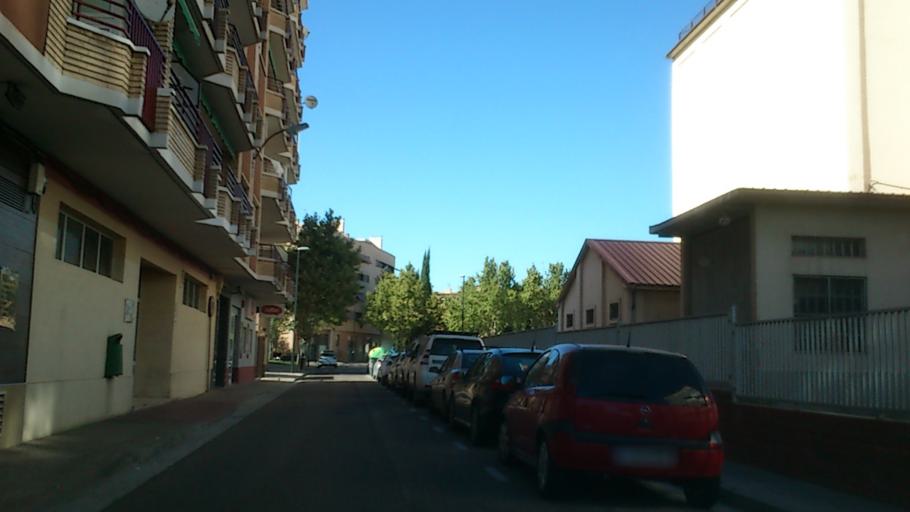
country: ES
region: Aragon
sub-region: Provincia de Zaragoza
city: Zaragoza
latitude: 41.6676
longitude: -0.8339
